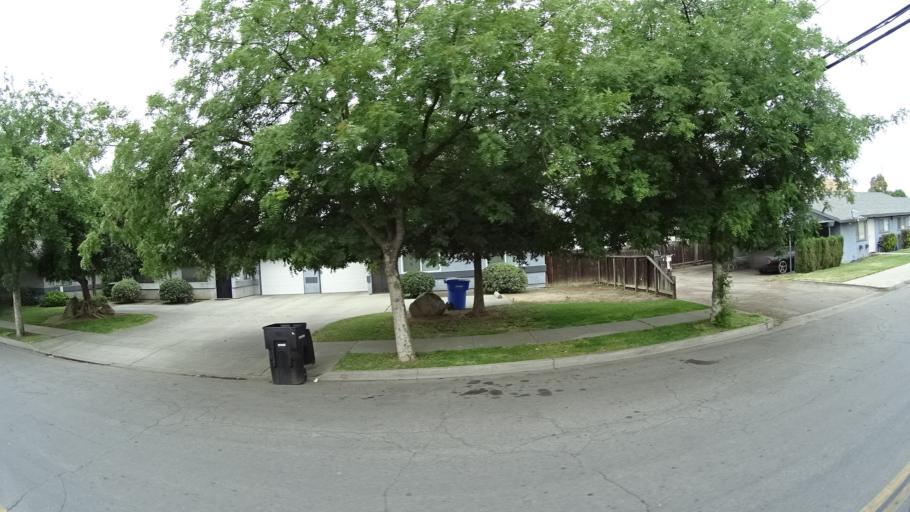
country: US
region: California
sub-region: Kings County
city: Hanford
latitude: 36.3304
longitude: -119.6427
